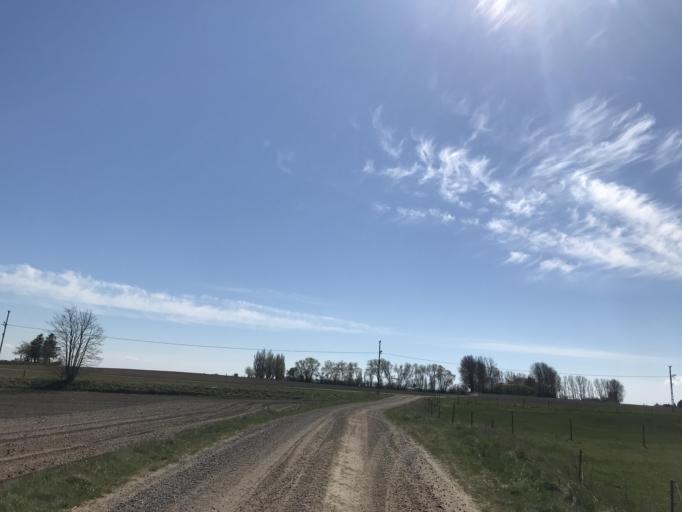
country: SE
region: Skane
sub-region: Landskrona
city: Asmundtorp
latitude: 55.8816
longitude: 12.9210
